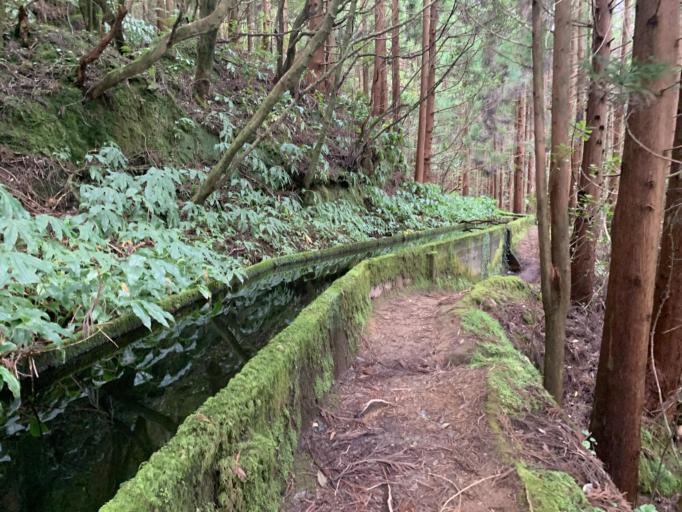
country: PT
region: Azores
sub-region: Vila Franca do Campo
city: Vila Franca do Campo
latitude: 37.7436
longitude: -25.4749
